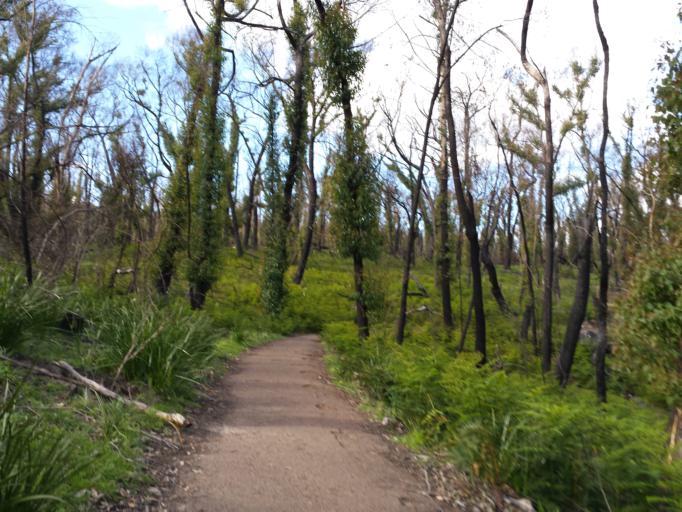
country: AU
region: Victoria
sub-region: Northern Grampians
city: Stawell
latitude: -37.1085
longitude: 142.4095
